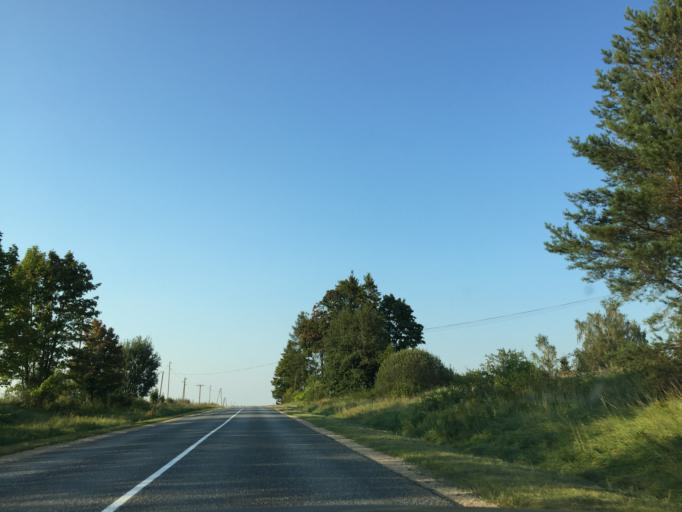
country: LV
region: Limbazu Rajons
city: Limbazi
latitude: 57.5705
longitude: 24.7696
